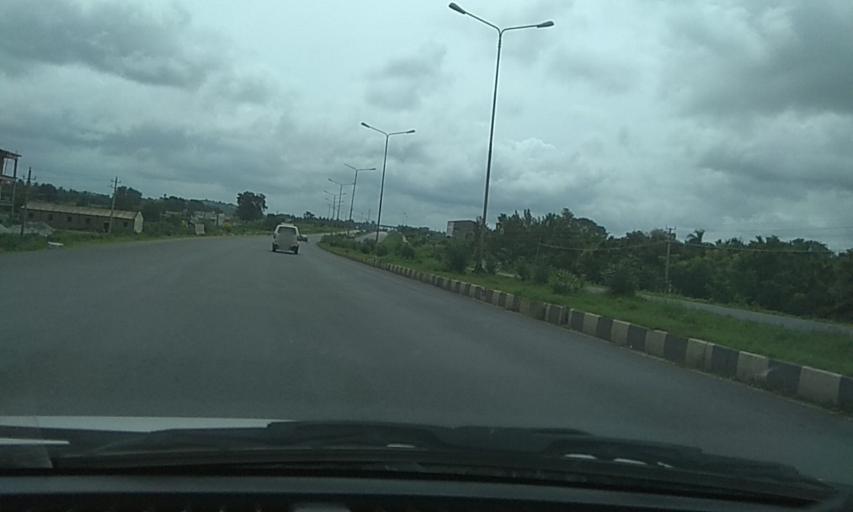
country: IN
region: Karnataka
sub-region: Davanagere
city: Mayakonda
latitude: 14.3776
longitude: 76.0989
